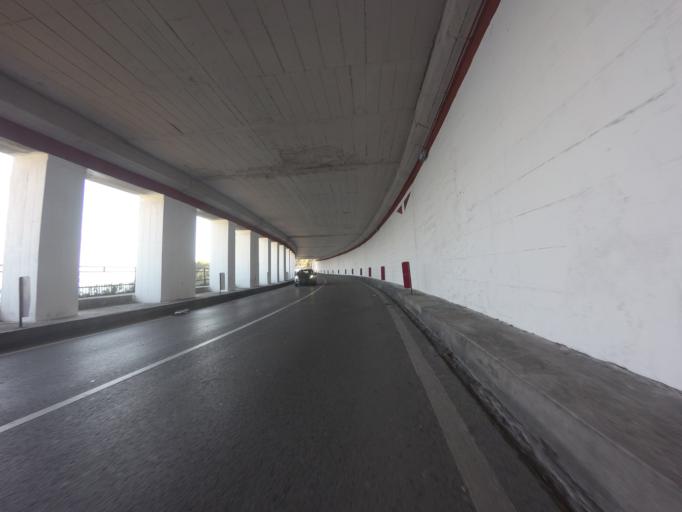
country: IT
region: Sicily
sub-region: Messina
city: Taormina
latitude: 37.8504
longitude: 15.2965
